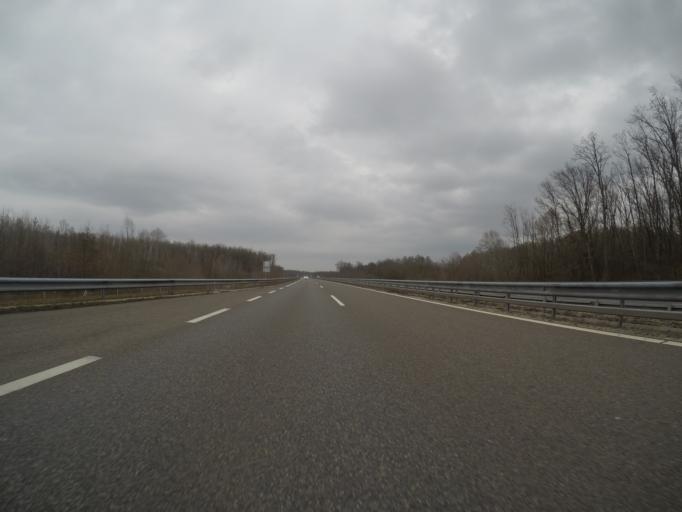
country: SI
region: Velika Polana
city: Velika Polana
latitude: 46.5976
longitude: 16.3801
